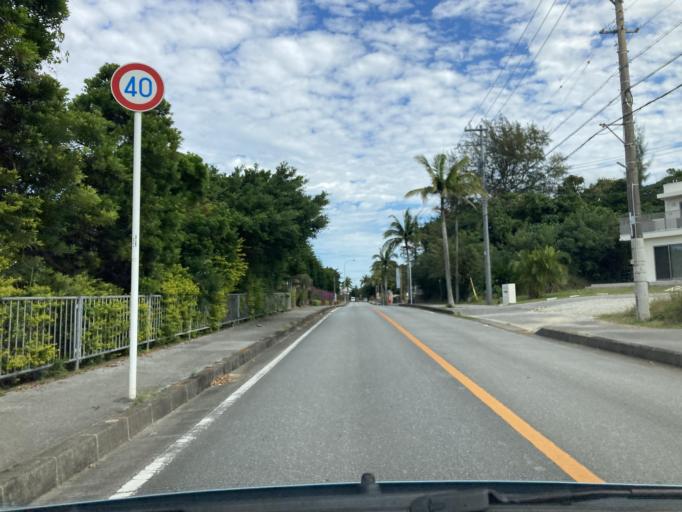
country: JP
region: Okinawa
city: Ishikawa
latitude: 26.4249
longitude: 127.7472
